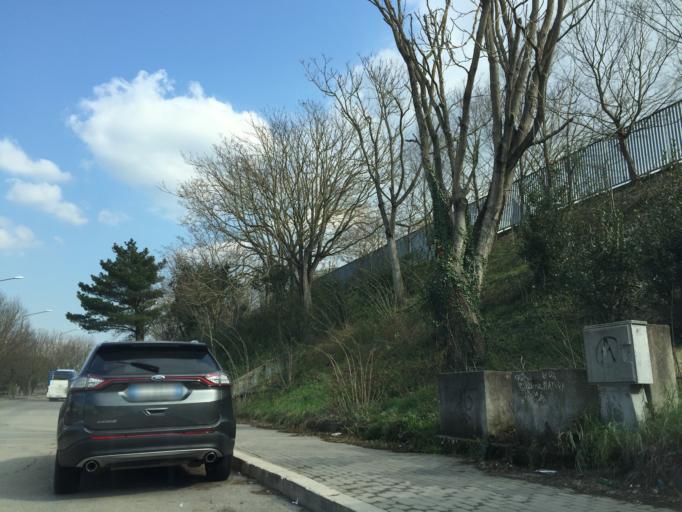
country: IT
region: Campania
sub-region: Provincia di Benevento
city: Benevento
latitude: 41.1319
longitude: 14.7839
